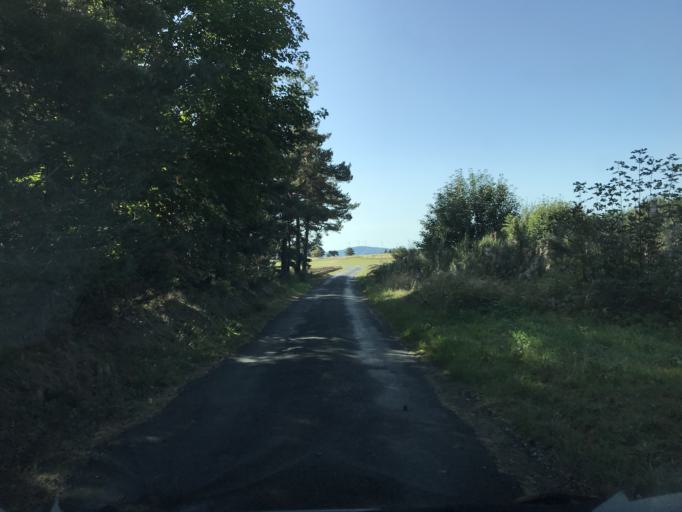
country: FR
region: Rhone-Alpes
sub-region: Departement de l'Ardeche
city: Saint-Agreve
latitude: 45.0335
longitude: 4.4444
